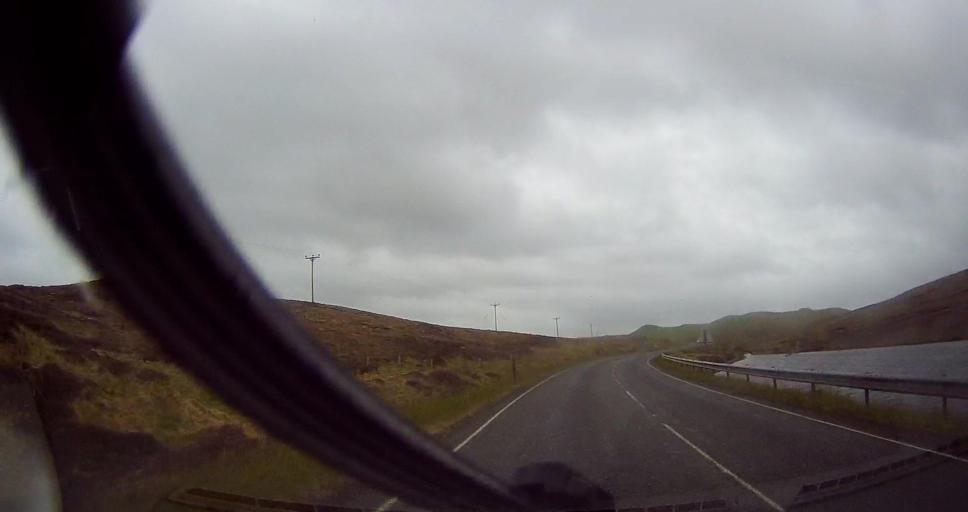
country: GB
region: Scotland
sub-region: Shetland Islands
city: Lerwick
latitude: 60.4375
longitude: -1.3972
